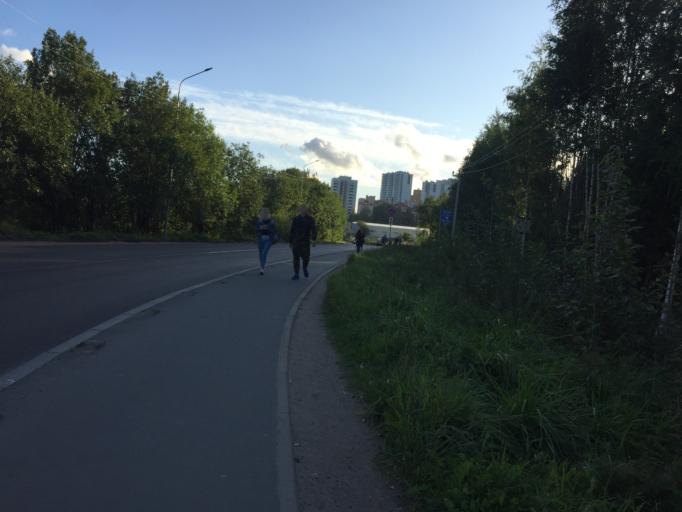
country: RU
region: Leningrad
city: Murino
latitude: 60.0566
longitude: 30.4597
